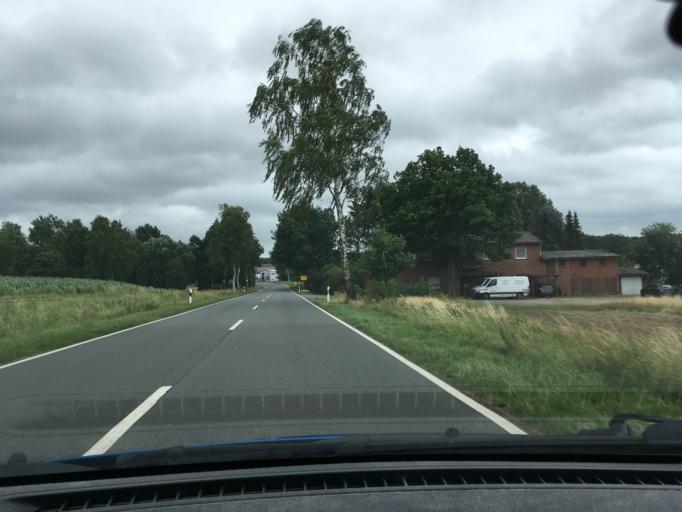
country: DE
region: Lower Saxony
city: Bispingen
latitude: 53.0939
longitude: 9.9848
